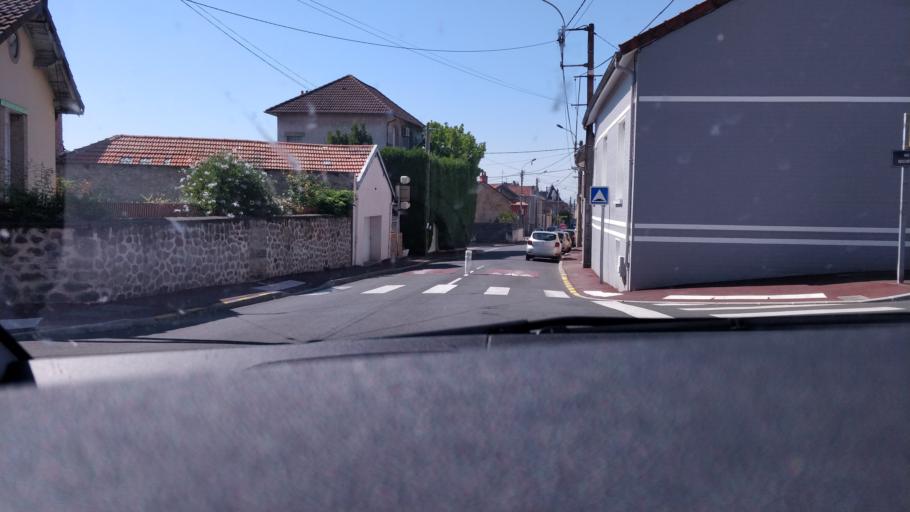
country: FR
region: Limousin
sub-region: Departement de la Haute-Vienne
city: Limoges
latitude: 45.8486
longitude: 1.2494
